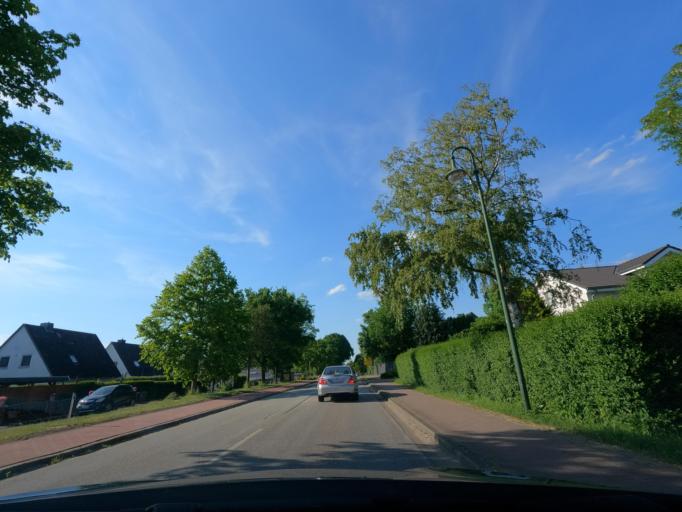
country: DE
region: Schleswig-Holstein
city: Gross Nordende
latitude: 53.7070
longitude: 9.6481
